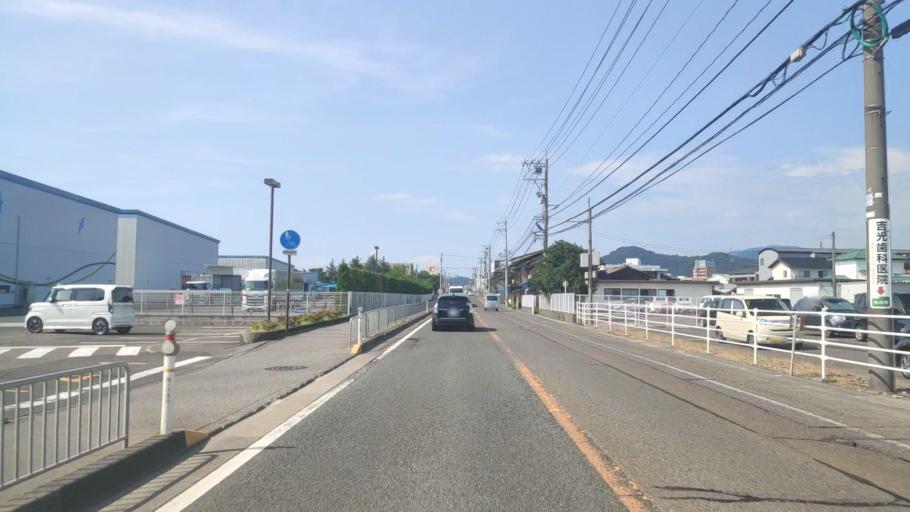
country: JP
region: Fukui
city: Tsuruga
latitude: 35.6399
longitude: 136.0709
